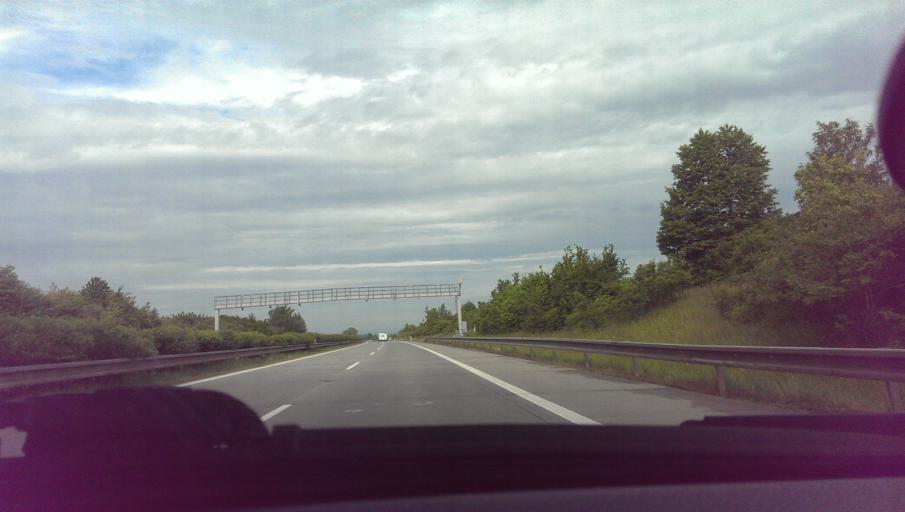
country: CZ
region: Olomoucky
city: Nezamyslice
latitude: 49.3183
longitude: 17.1704
